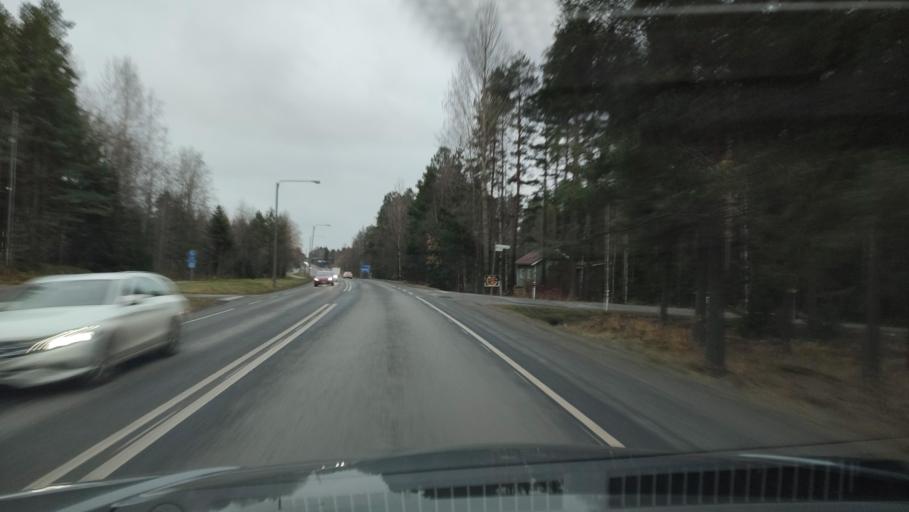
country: FI
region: Southern Ostrobothnia
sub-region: Seinaejoki
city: Ilmajoki
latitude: 62.7748
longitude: 22.6866
